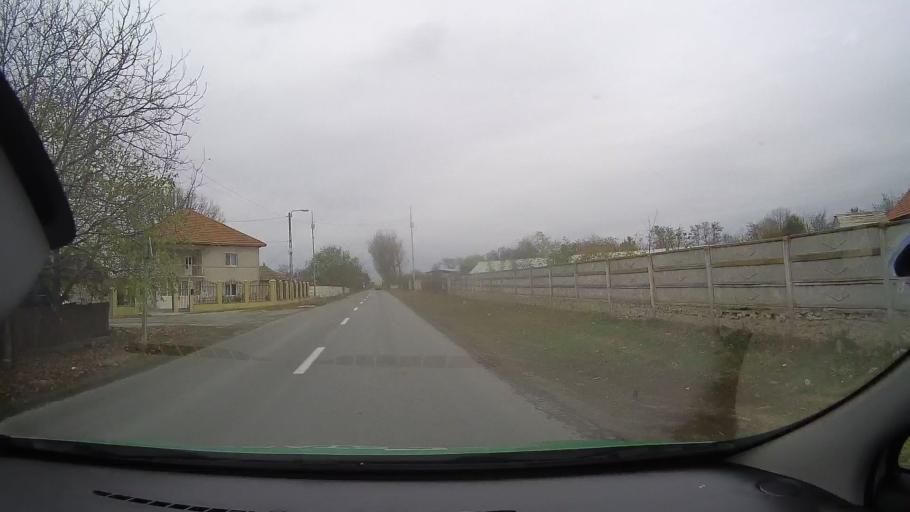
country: RO
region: Constanta
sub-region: Comuna Mihail Kogalniceanu
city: Mihail Kogalniceanu
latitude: 44.3792
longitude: 28.4649
